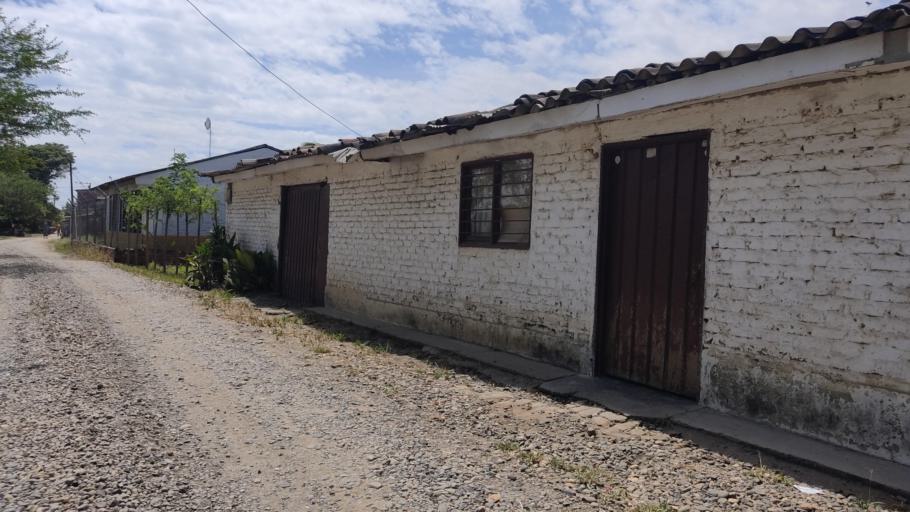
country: CO
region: Valle del Cauca
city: Jamundi
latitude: 3.1605
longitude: -76.5122
